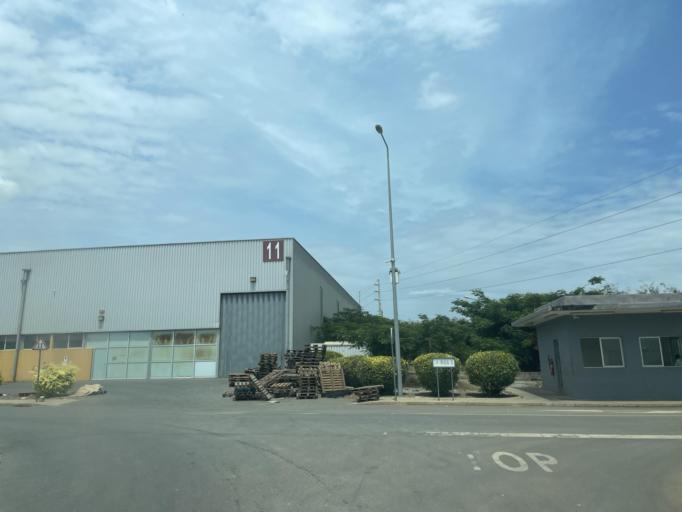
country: AO
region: Luanda
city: Luanda
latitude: -8.9604
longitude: 13.3917
